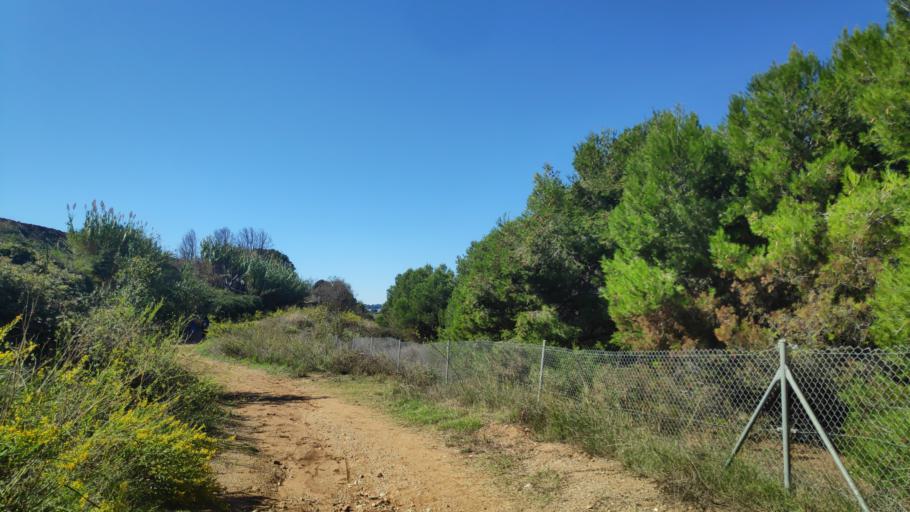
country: ES
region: Catalonia
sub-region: Provincia de Barcelona
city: Santa Perpetua de Mogoda
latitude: 41.5444
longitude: 2.1935
